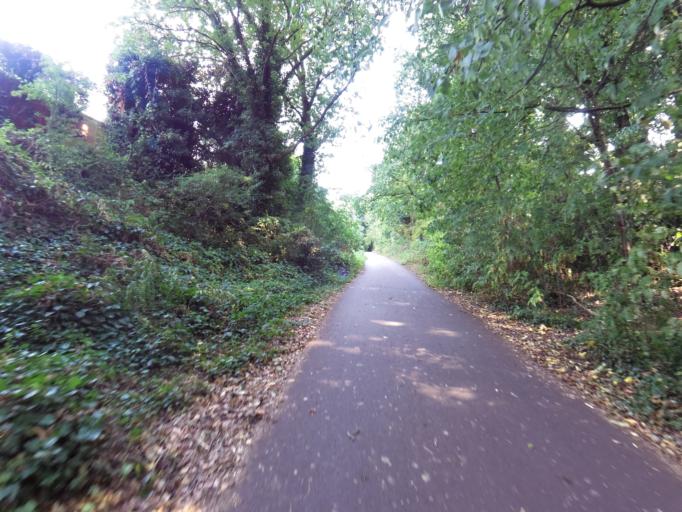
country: GB
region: England
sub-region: Hertfordshire
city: St Albans
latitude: 51.7499
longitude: -0.3039
